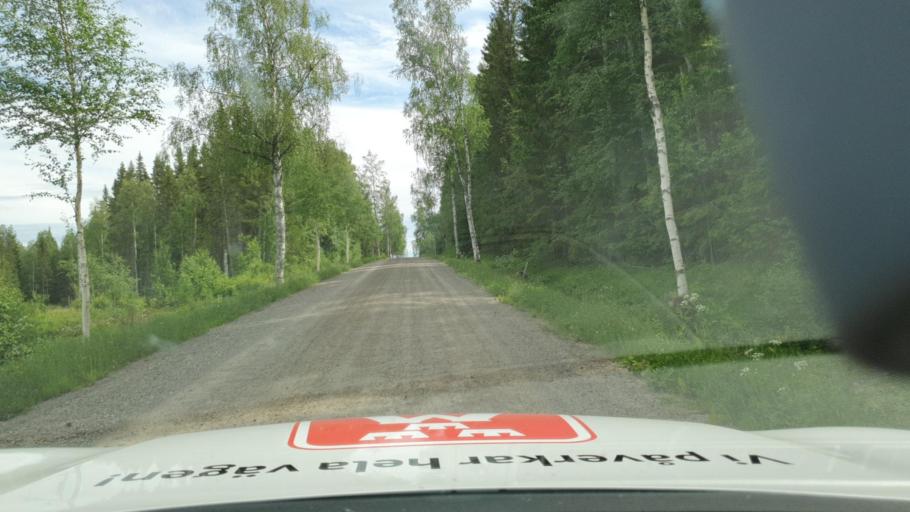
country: SE
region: Vaesterbotten
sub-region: Skelleftea Kommun
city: Burtraesk
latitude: 64.4763
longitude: 20.4424
